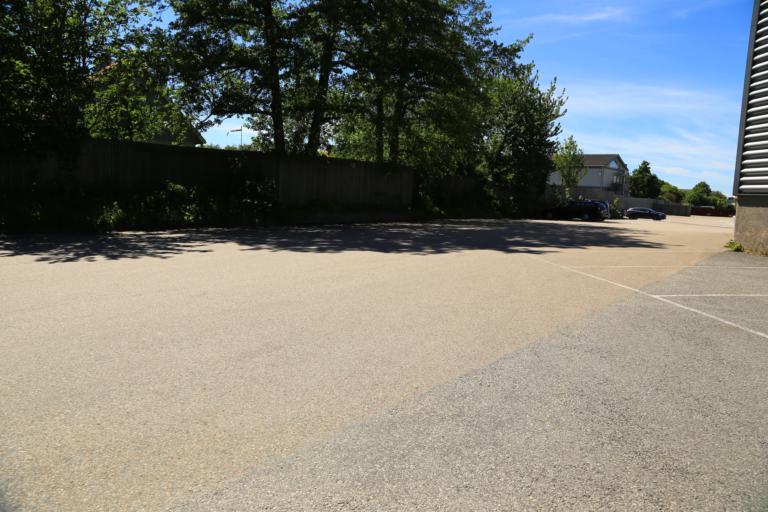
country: SE
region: Halland
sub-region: Varbergs Kommun
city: Varberg
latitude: 57.1018
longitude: 12.2692
